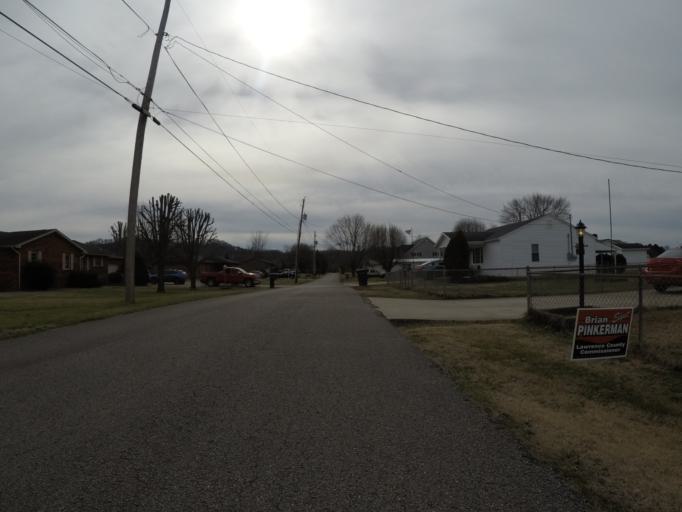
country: US
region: West Virginia
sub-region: Cabell County
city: Pea Ridge
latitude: 38.4520
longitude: -82.3348
